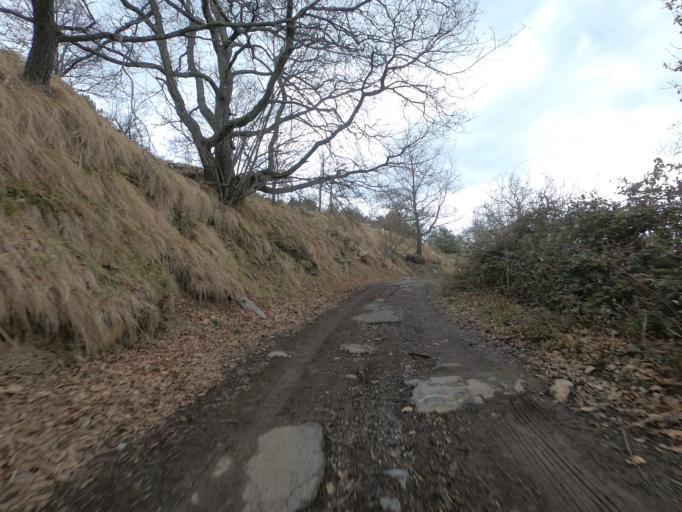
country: IT
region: Liguria
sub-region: Provincia di Imperia
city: Badalucco
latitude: 43.9165
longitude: 7.8797
